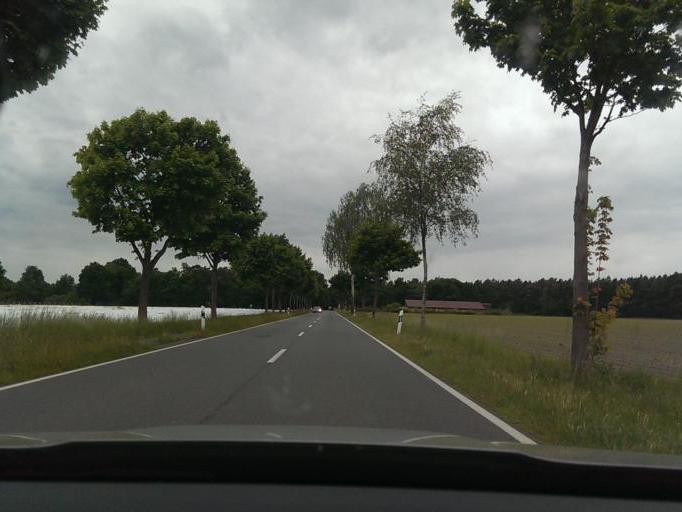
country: DE
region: Lower Saxony
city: Essel
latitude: 52.6880
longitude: 9.7104
